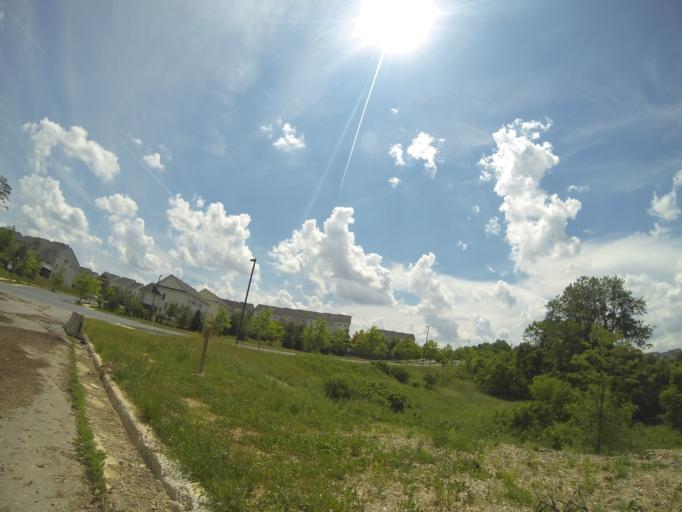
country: US
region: Maryland
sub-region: Montgomery County
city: Clarksburg
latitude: 39.2396
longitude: -77.2733
